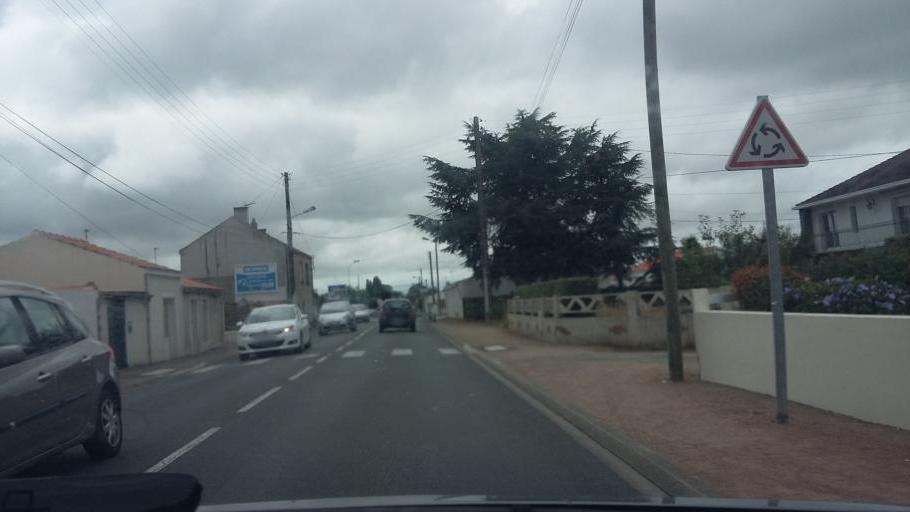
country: FR
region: Pays de la Loire
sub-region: Departement de la Vendee
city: Challans
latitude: 46.8419
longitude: -1.8939
